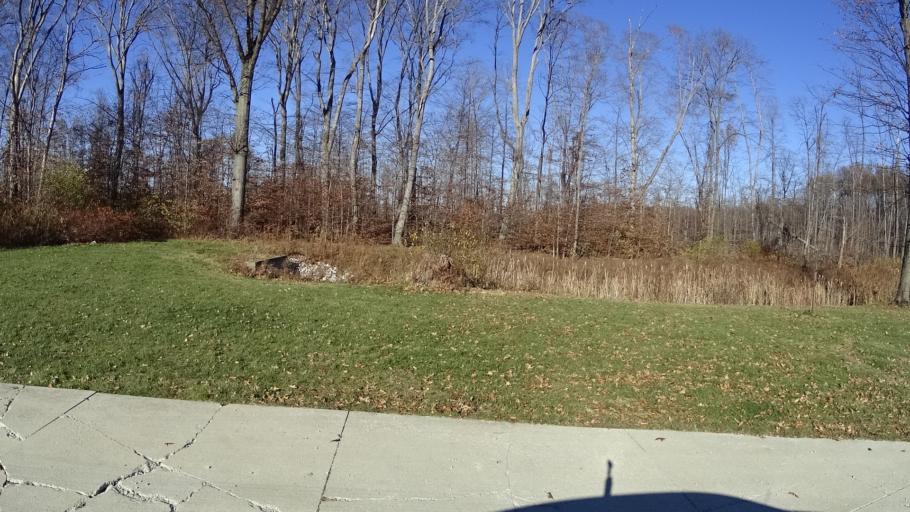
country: US
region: Ohio
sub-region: Lorain County
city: Avon Center
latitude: 41.4447
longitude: -81.9800
